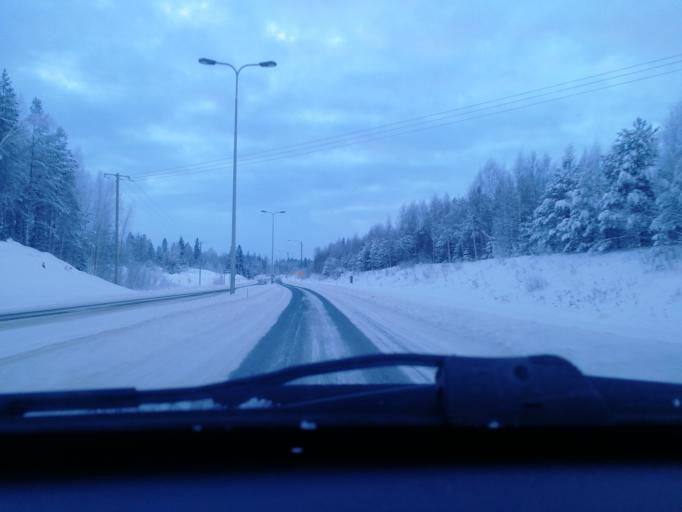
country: FI
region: Pirkanmaa
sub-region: Tampere
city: Tampere
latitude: 61.4413
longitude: 23.8760
